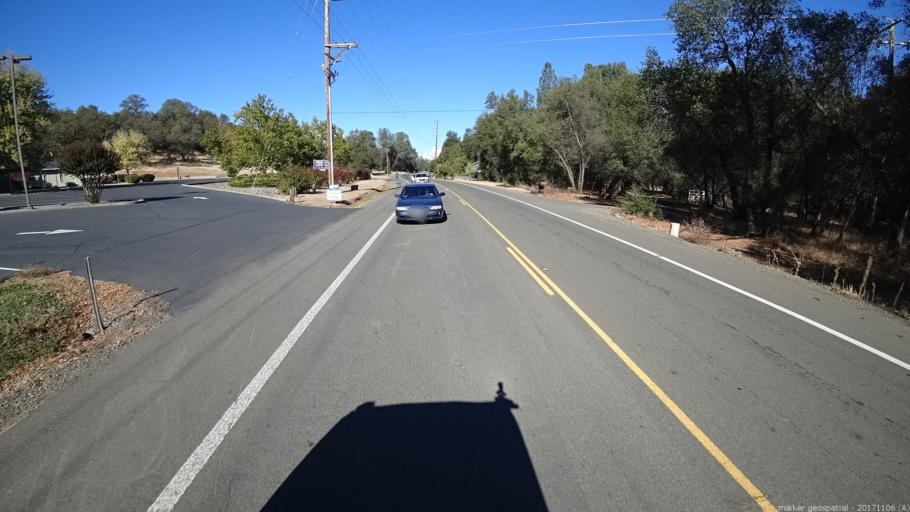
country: US
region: California
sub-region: Shasta County
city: Palo Cedro
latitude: 40.5948
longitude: -122.3103
